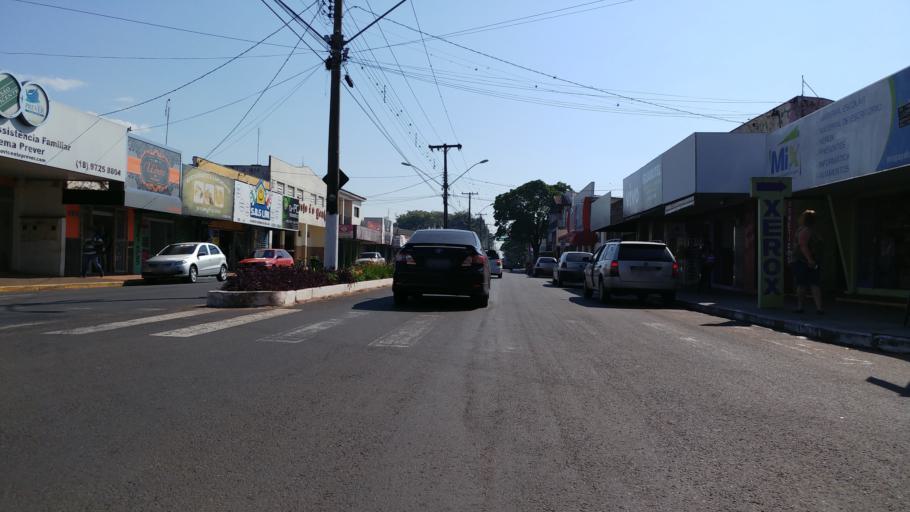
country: BR
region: Sao Paulo
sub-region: Paraguacu Paulista
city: Paraguacu Paulista
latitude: -22.4233
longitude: -50.5816
